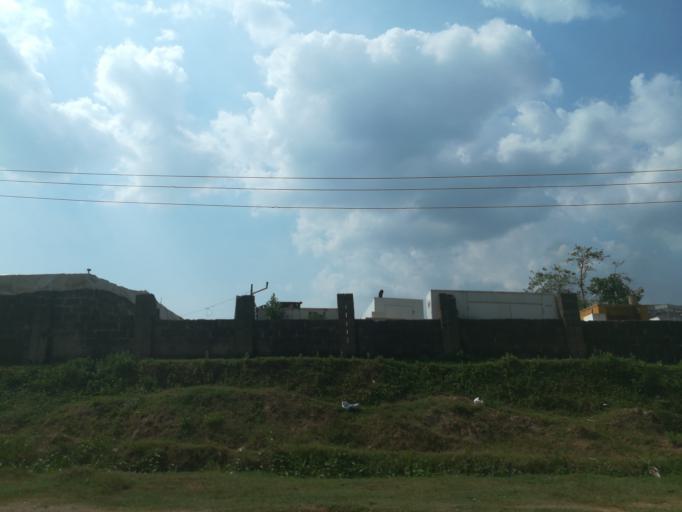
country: NG
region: Abuja Federal Capital Territory
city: Abuja
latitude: 9.0602
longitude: 7.4355
